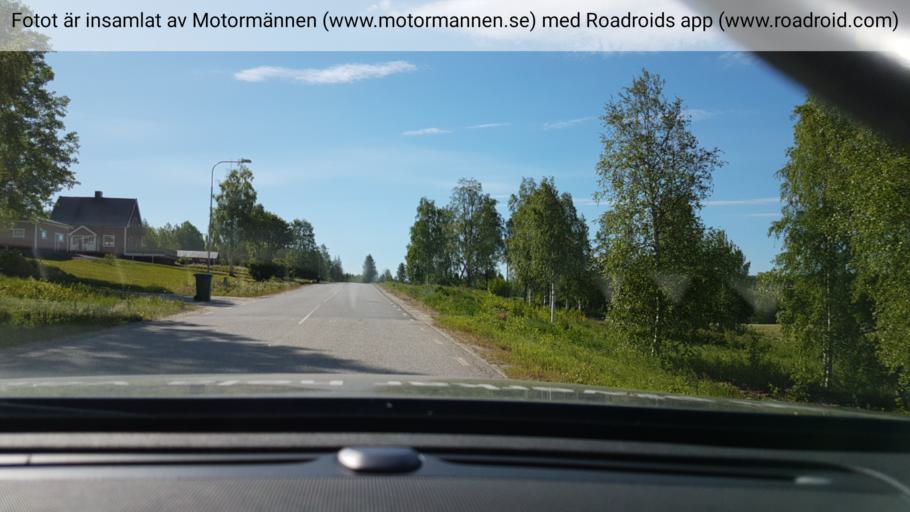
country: SE
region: Vaesterbotten
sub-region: Bjurholms Kommun
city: Bjurholm
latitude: 64.0228
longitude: 19.3474
